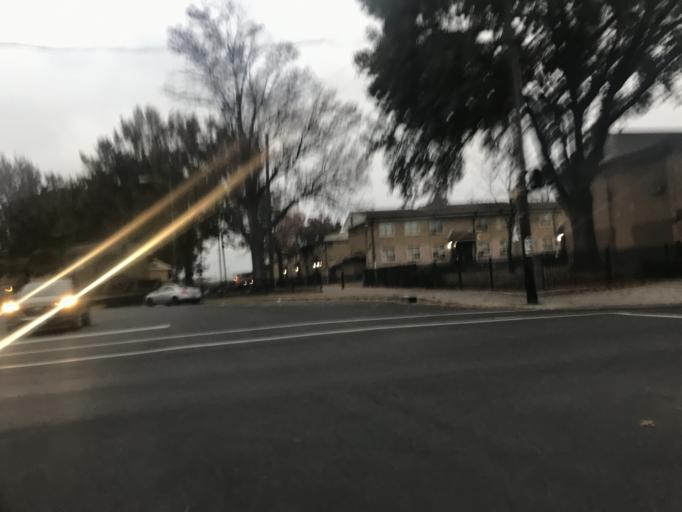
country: US
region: Kentucky
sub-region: Jefferson County
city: Louisville
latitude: 38.2275
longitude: -85.7752
